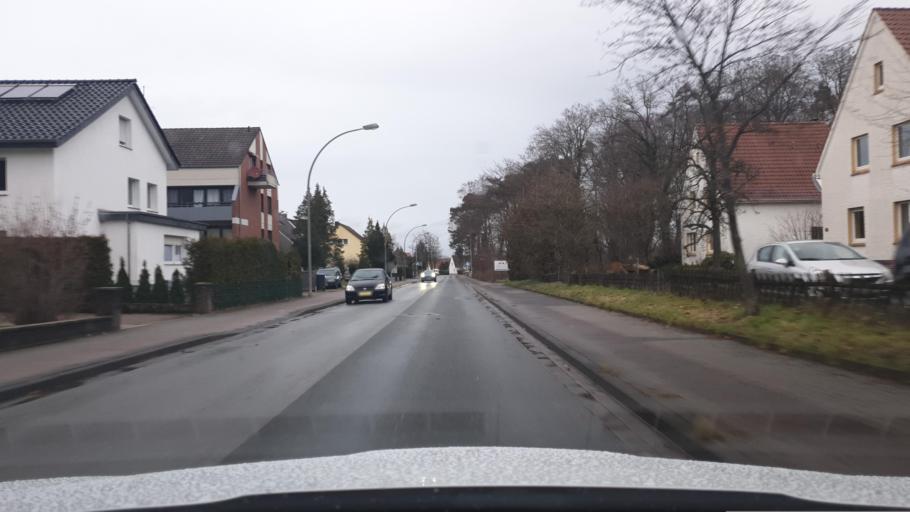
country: DE
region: North Rhine-Westphalia
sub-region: Regierungsbezirk Detmold
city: Lage
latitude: 51.9468
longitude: 8.8107
